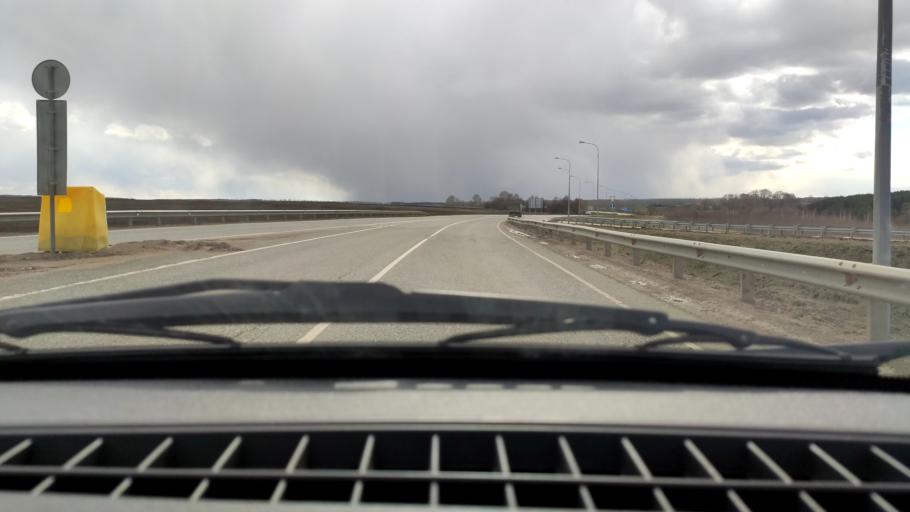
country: RU
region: Bashkortostan
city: Kushnarenkovo
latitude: 55.0755
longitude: 55.2726
